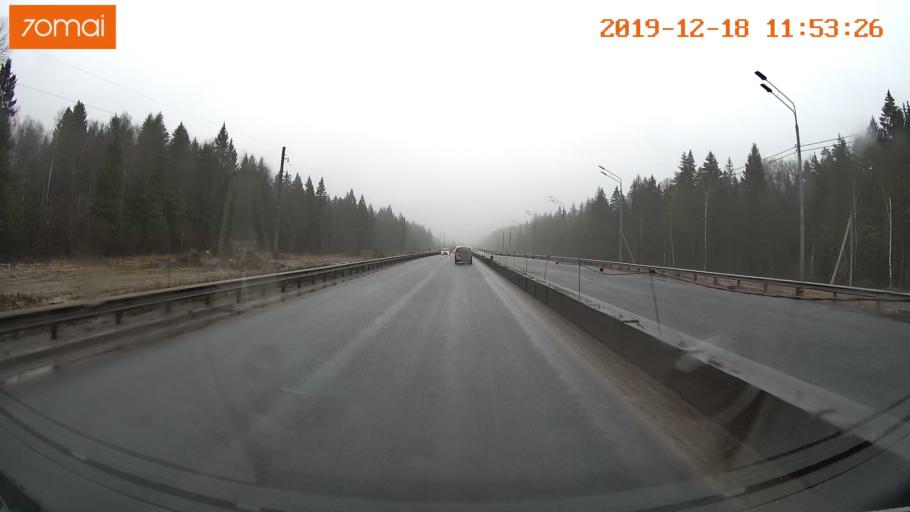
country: RU
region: Moskovskaya
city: Yershovo
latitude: 55.8043
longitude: 36.9199
